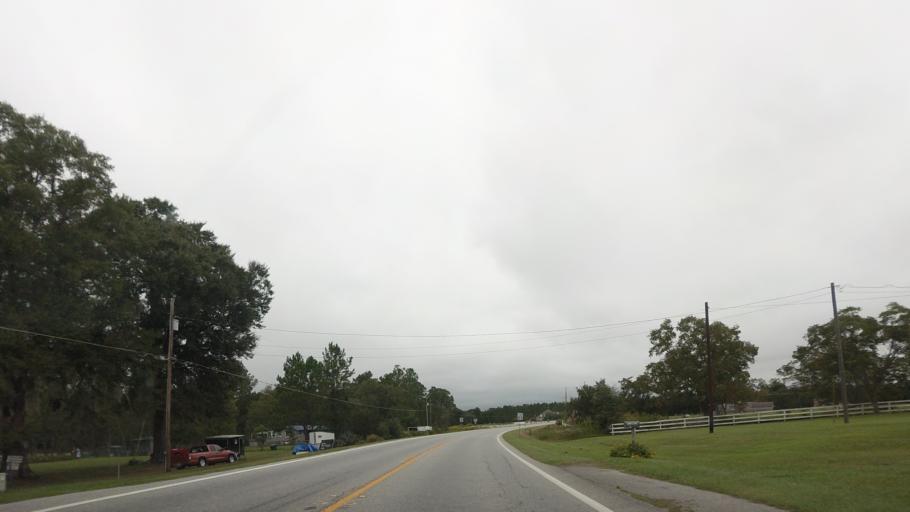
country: US
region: Georgia
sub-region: Berrien County
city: Ray City
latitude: 31.0802
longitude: -83.2047
